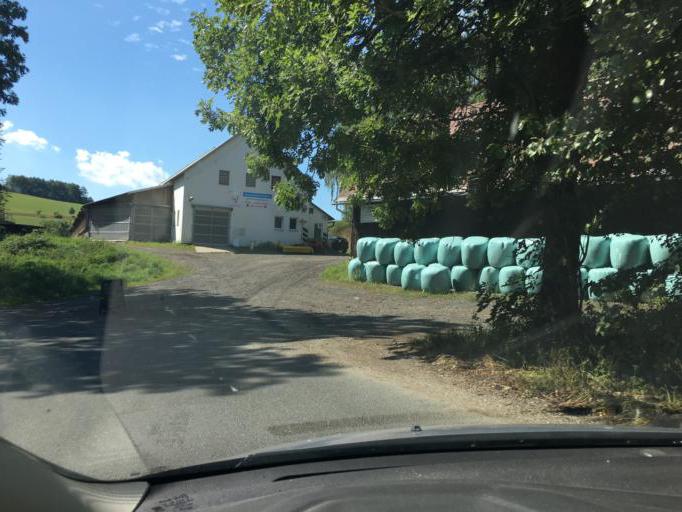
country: CZ
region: Liberecky
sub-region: Okres Semily
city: Vysoke nad Jizerou
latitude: 50.7035
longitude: 15.3657
